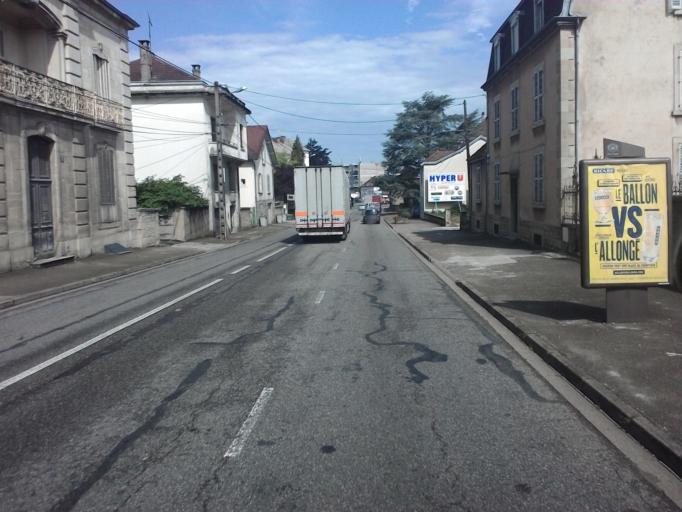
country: FR
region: Franche-Comte
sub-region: Departement du Jura
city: Lons-le-Saunier
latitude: 46.6711
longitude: 5.5447
